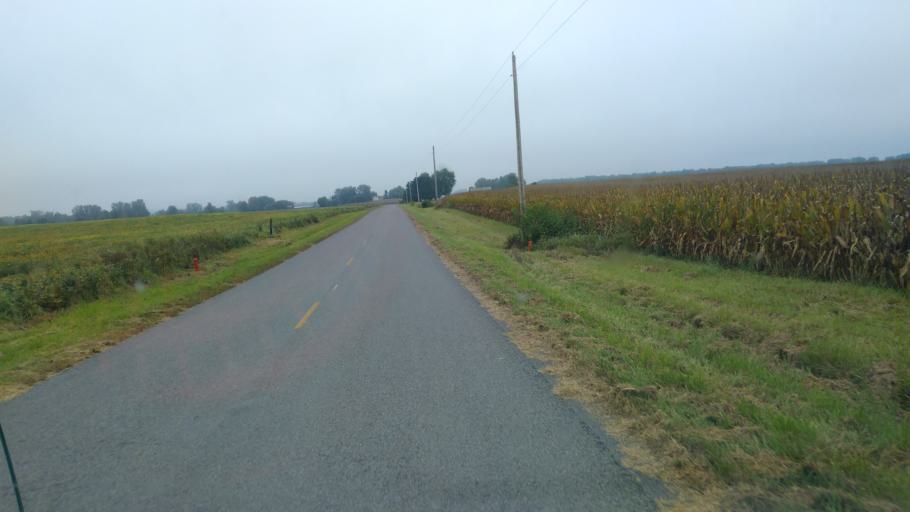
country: US
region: Ohio
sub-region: Logan County
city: Northwood
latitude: 40.4789
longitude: -83.5846
